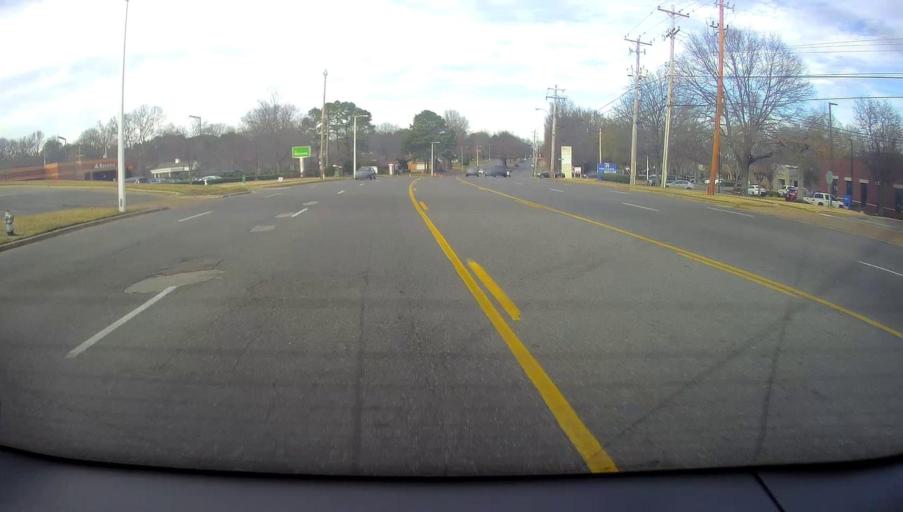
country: US
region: Tennessee
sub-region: Shelby County
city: Germantown
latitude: 35.0515
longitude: -89.8443
